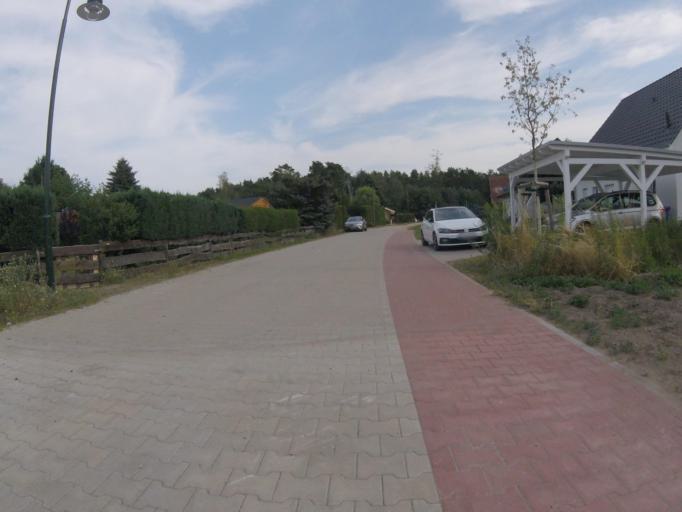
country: DE
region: Brandenburg
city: Spreenhagen
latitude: 52.3012
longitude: 13.8026
